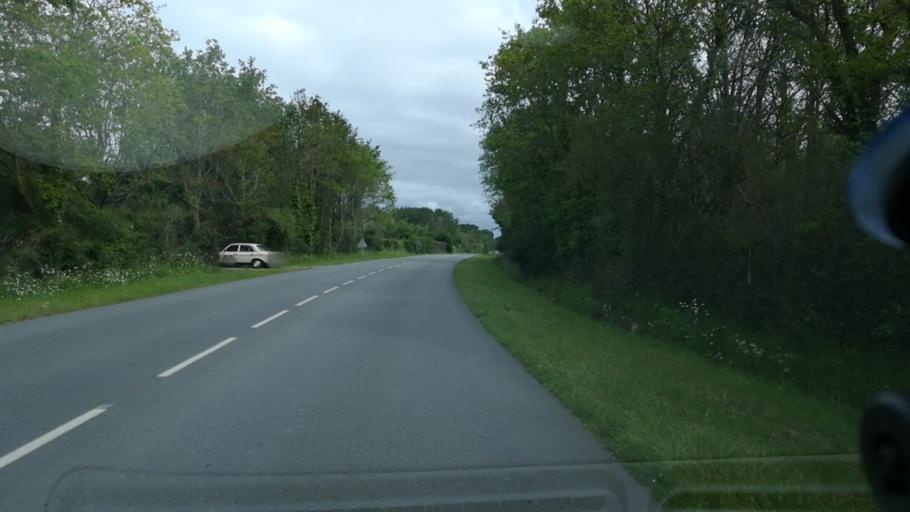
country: FR
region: Brittany
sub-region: Departement du Morbihan
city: Penestin
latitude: 47.4607
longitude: -2.4774
